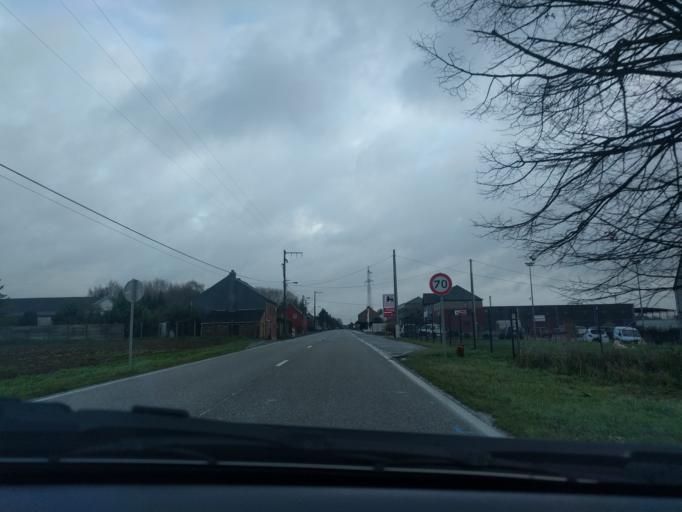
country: BE
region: Wallonia
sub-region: Province de Namur
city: Noville-les-Bois
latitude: 50.5210
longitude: 4.9933
